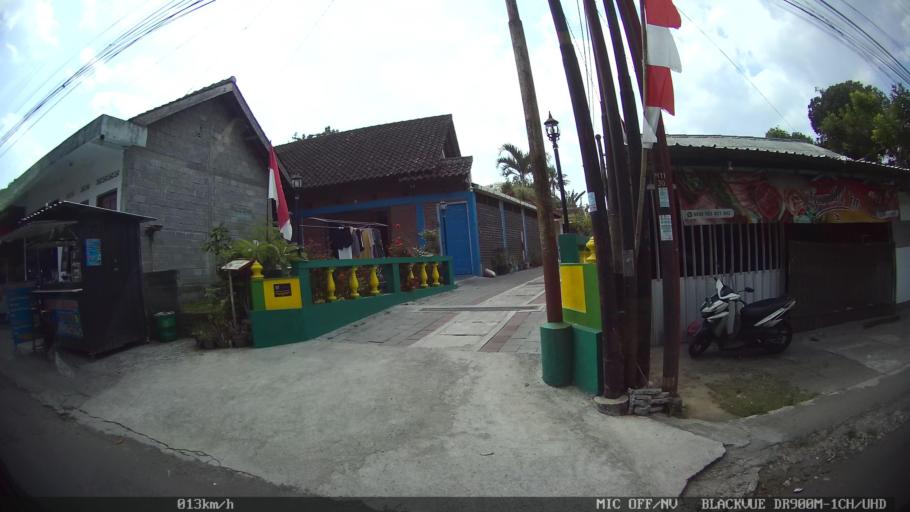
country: ID
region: Daerah Istimewa Yogyakarta
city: Kasihan
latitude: -7.8143
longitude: 110.3332
